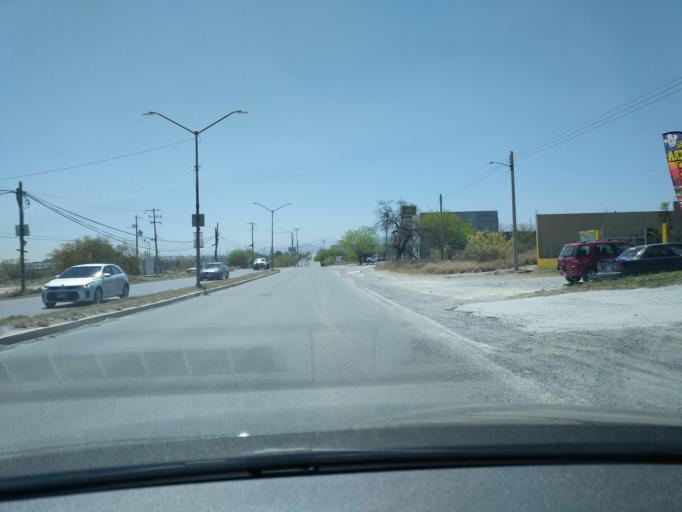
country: MX
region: Nuevo Leon
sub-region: Apodaca
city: Artemio Trevino
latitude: 25.8030
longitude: -100.1562
